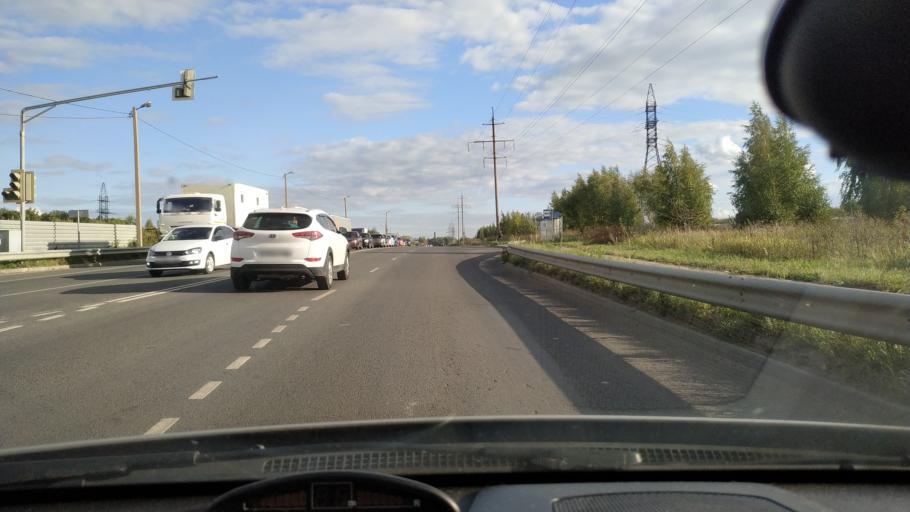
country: RU
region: Rjazan
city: Ryazan'
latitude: 54.5903
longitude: 39.8141
